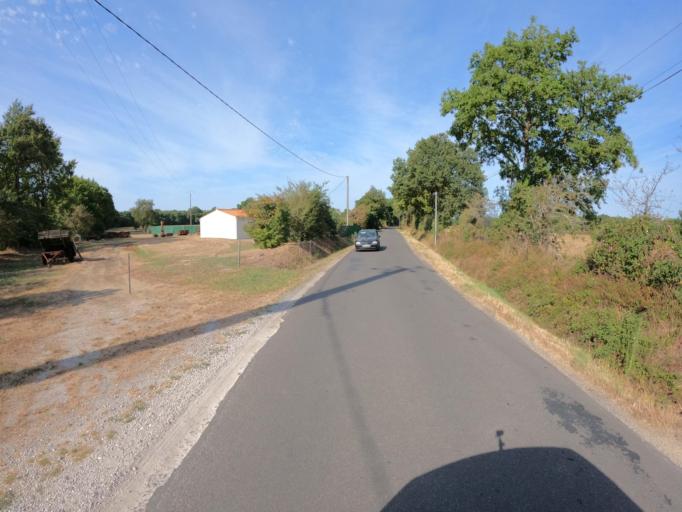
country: FR
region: Pays de la Loire
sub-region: Departement de la Vendee
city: Challans
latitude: 46.8078
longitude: -1.8456
